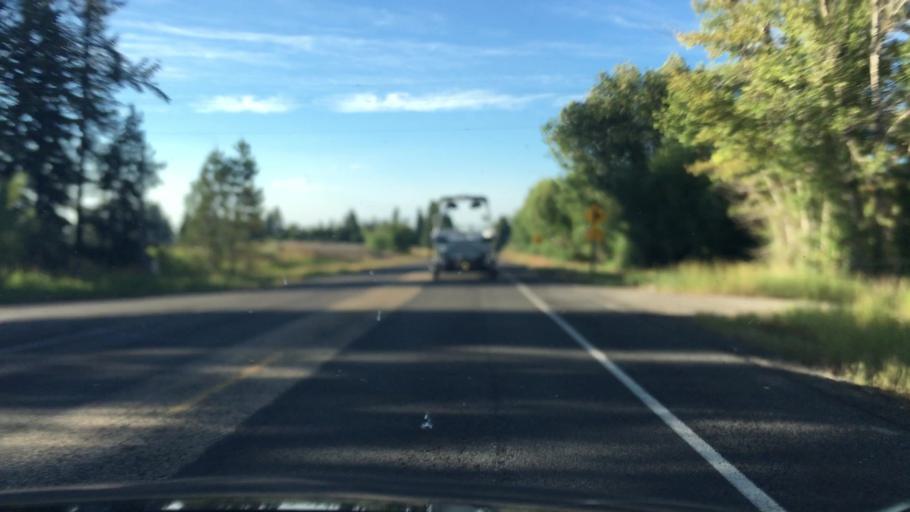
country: US
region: Idaho
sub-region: Valley County
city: Cascade
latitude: 44.6833
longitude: -116.0519
